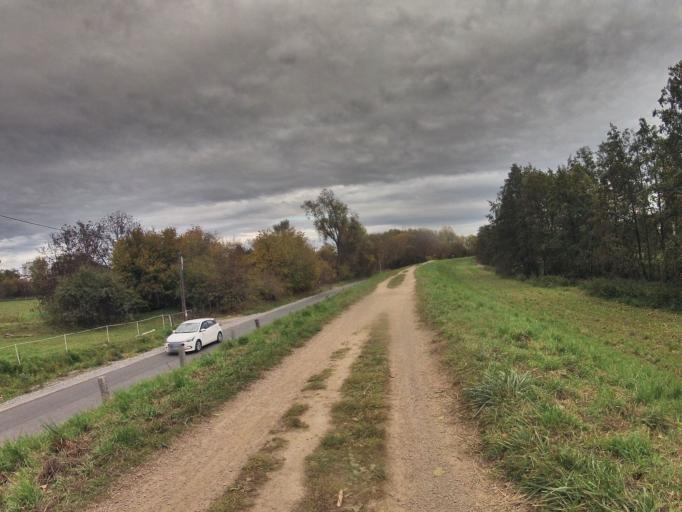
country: PL
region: Lesser Poland Voivodeship
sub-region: Krakow
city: Krakow
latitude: 50.0670
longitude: 19.8895
